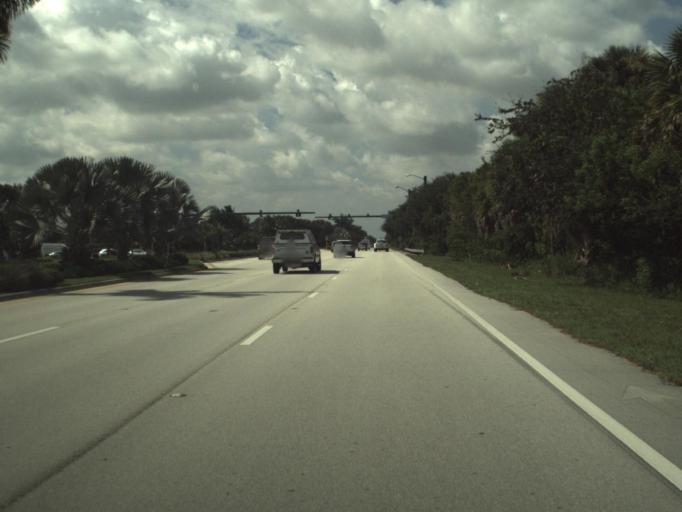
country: US
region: Florida
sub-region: Palm Beach County
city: Jupiter
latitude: 26.9056
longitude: -80.0946
